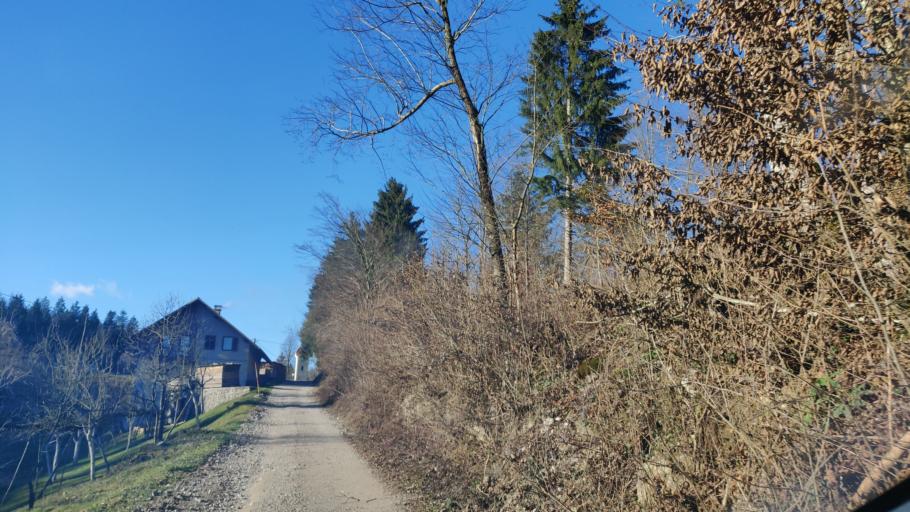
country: SI
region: Logatec
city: Logatec
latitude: 45.8718
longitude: 14.2158
